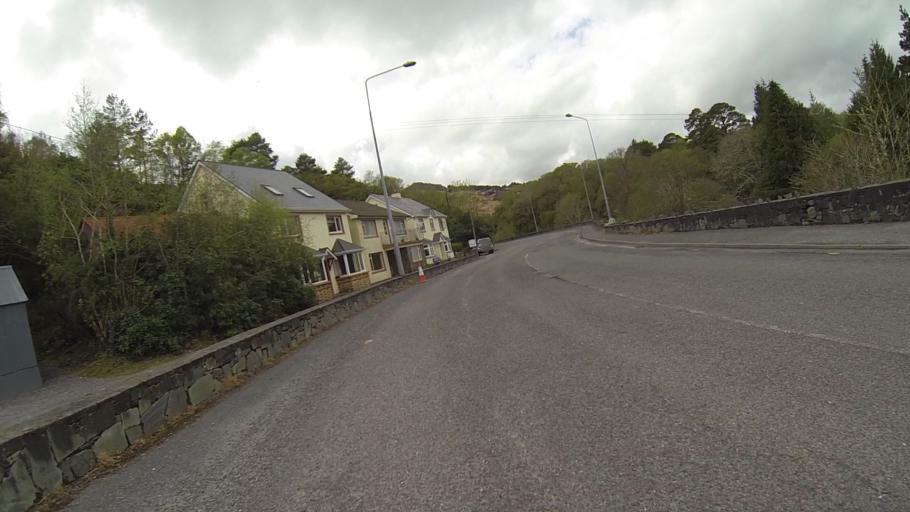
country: IE
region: Munster
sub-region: County Cork
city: Bantry
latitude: 51.7489
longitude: -9.5536
